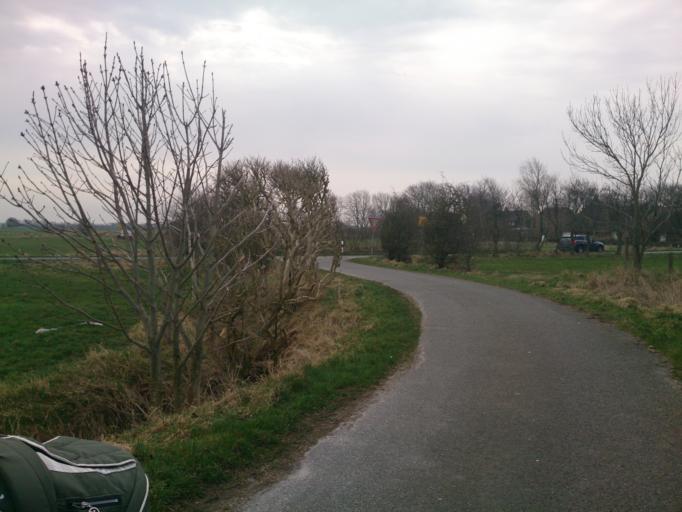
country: DE
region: Schleswig-Holstein
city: Utersum
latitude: 54.7167
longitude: 8.4077
